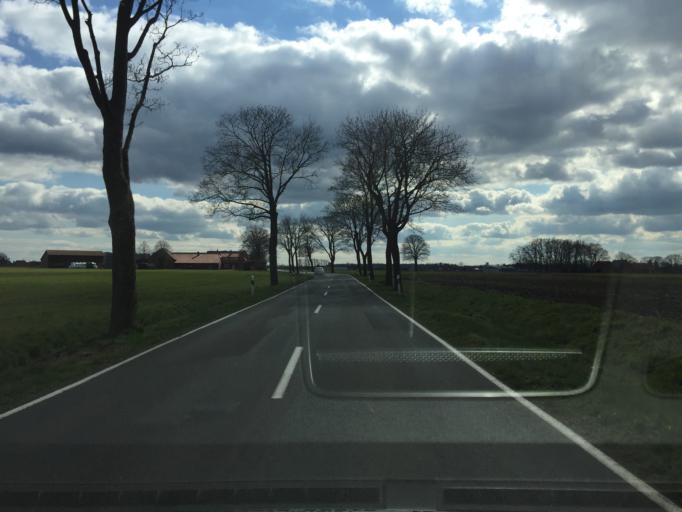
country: DE
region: Lower Saxony
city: Mellinghausen
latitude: 52.7195
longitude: 8.9083
